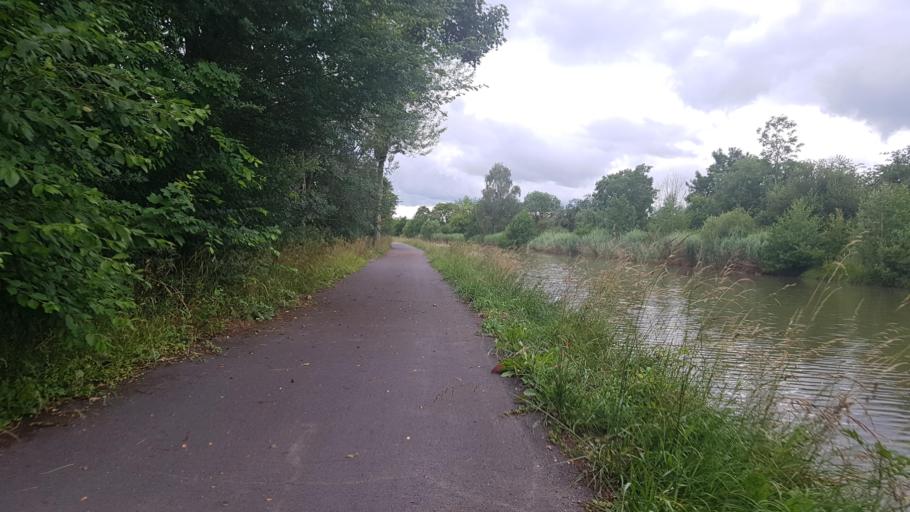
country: FR
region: Lorraine
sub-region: Departement de Meurthe-et-Moselle
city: Chanteheux
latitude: 48.6826
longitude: 6.6153
